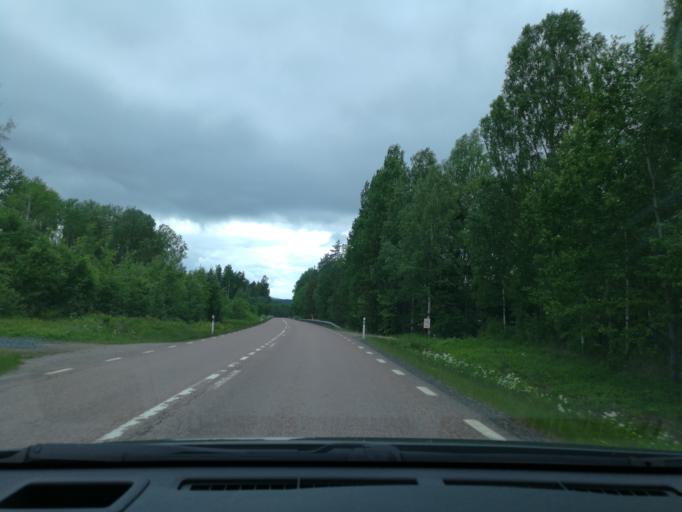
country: SE
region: Dalarna
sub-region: Smedjebackens Kommun
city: Smedjebacken
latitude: 60.1305
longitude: 15.4506
